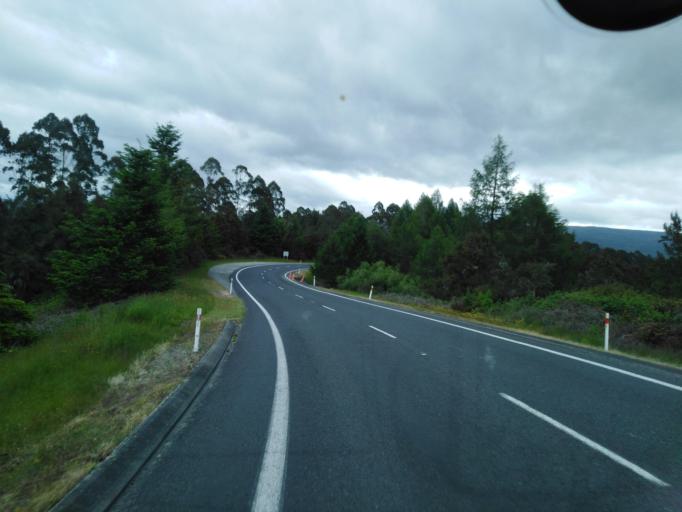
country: NZ
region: Tasman
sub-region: Tasman District
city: Wakefield
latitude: -41.6294
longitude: 172.7077
